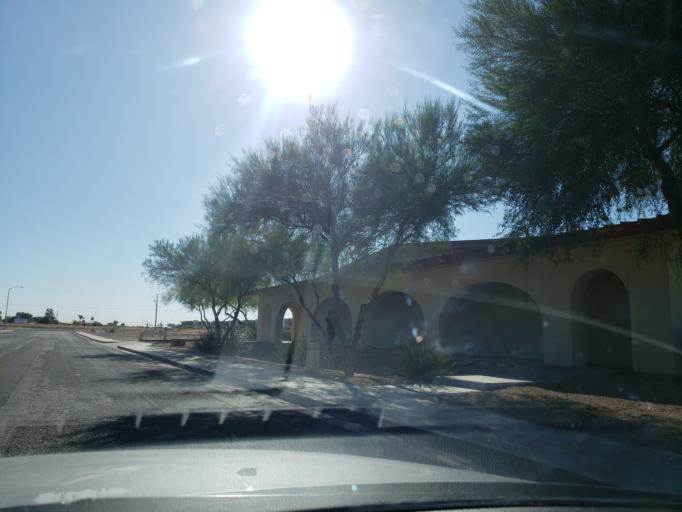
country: US
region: Arizona
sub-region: Maricopa County
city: Avondale
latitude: 33.4462
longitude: -112.3471
